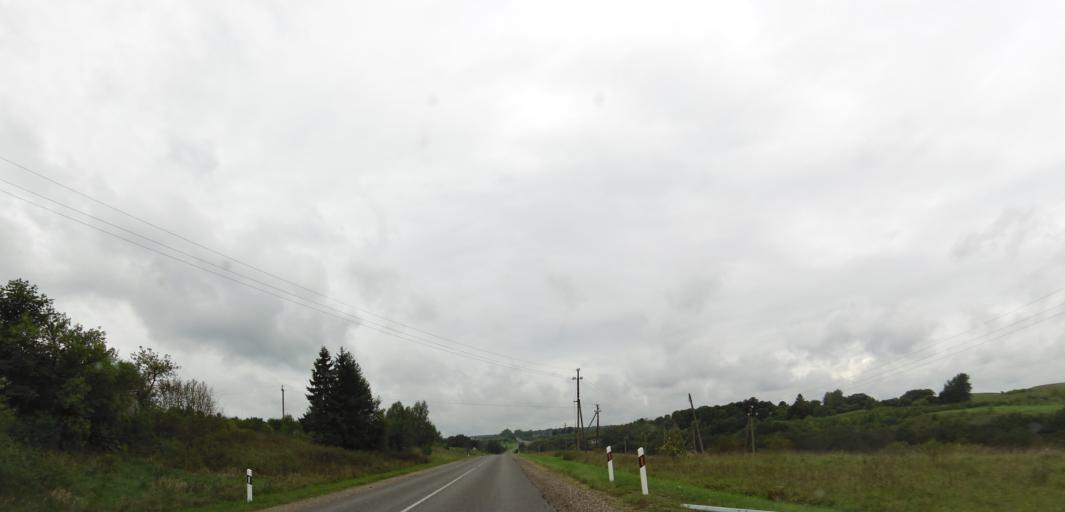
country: LT
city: Sirvintos
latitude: 55.2230
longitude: 25.1097
